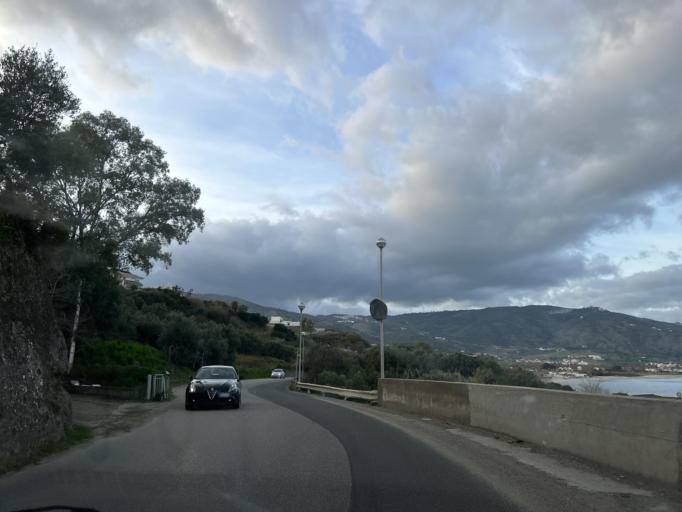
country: IT
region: Calabria
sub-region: Provincia di Catanzaro
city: Soverato Superiore
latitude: 38.6993
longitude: 16.5396
